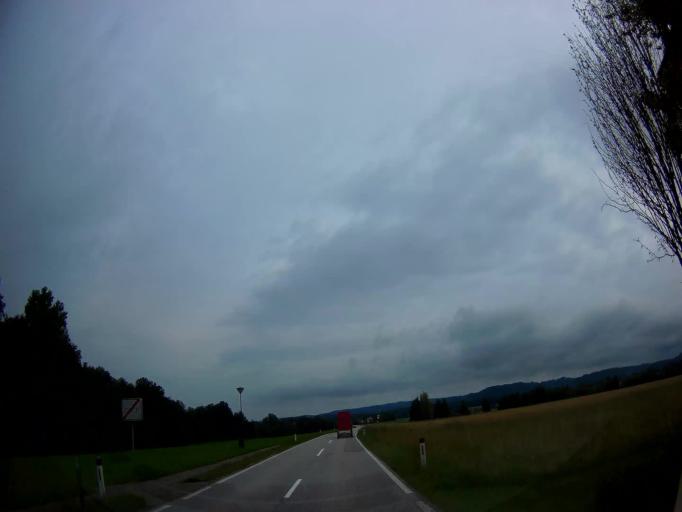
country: AT
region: Salzburg
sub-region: Politischer Bezirk Salzburg-Umgebung
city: Mattsee
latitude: 48.0425
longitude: 13.1482
